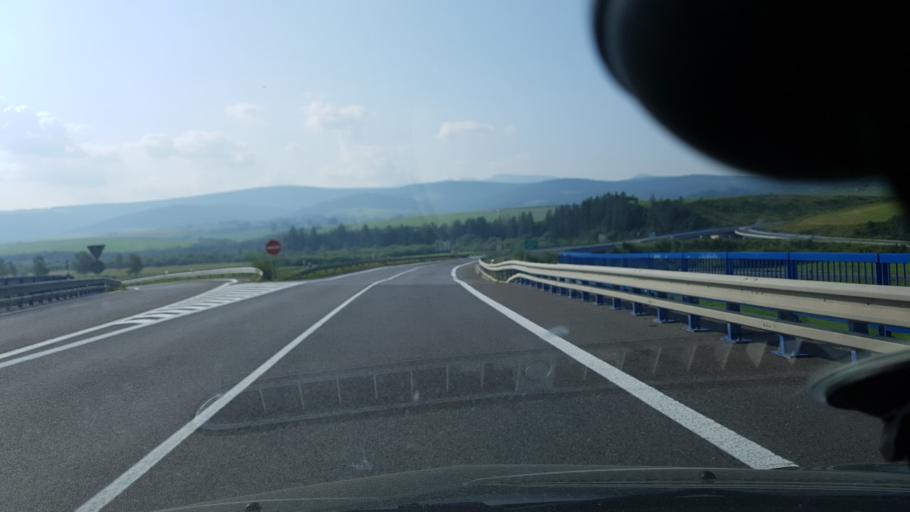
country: SK
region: Zilinsky
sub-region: Okres Zilina
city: Trstena
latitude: 49.3647
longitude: 19.6333
